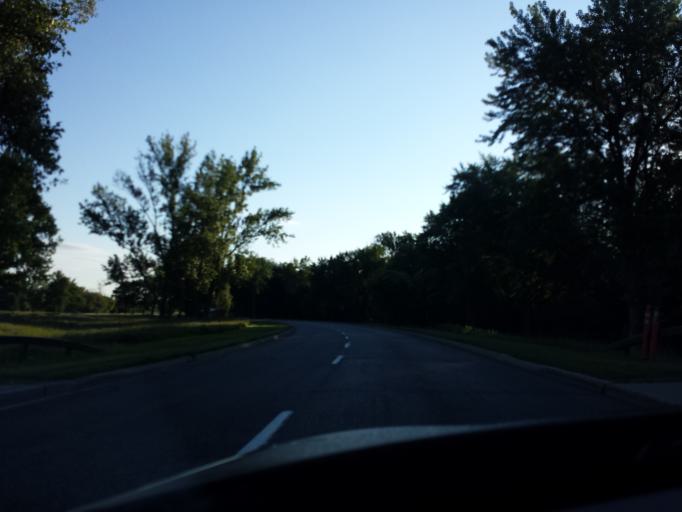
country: CA
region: Ontario
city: Bells Corners
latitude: 45.3760
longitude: -75.7803
